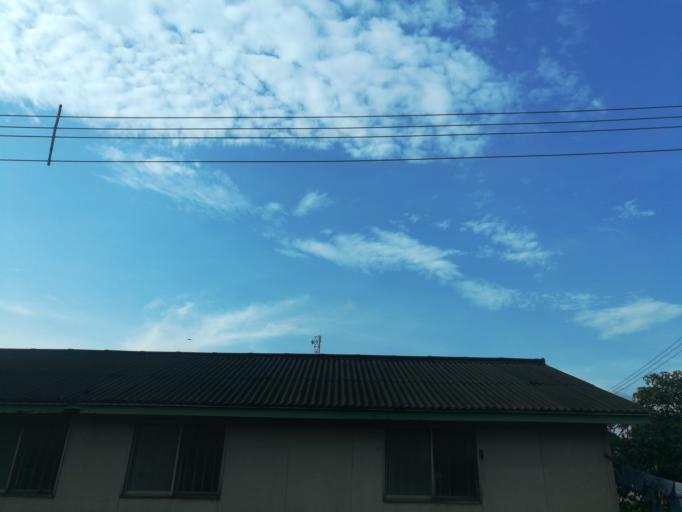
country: NG
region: Lagos
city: Ikeja
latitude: 6.5955
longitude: 3.3491
